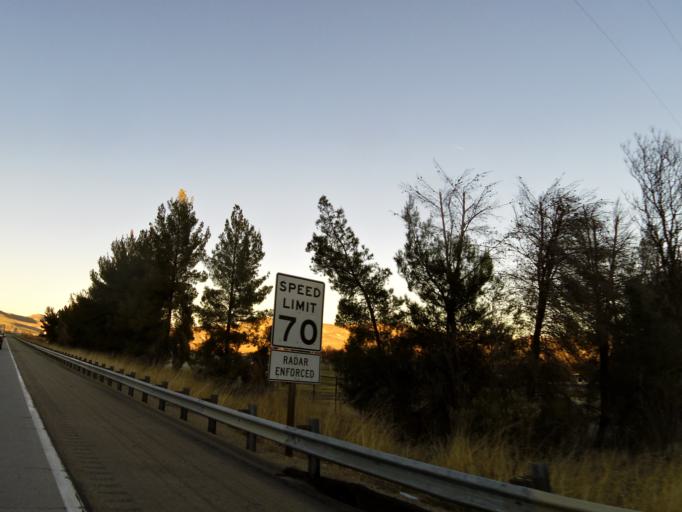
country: US
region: California
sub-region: San Luis Obispo County
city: San Miguel
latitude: 35.7557
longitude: -120.6991
